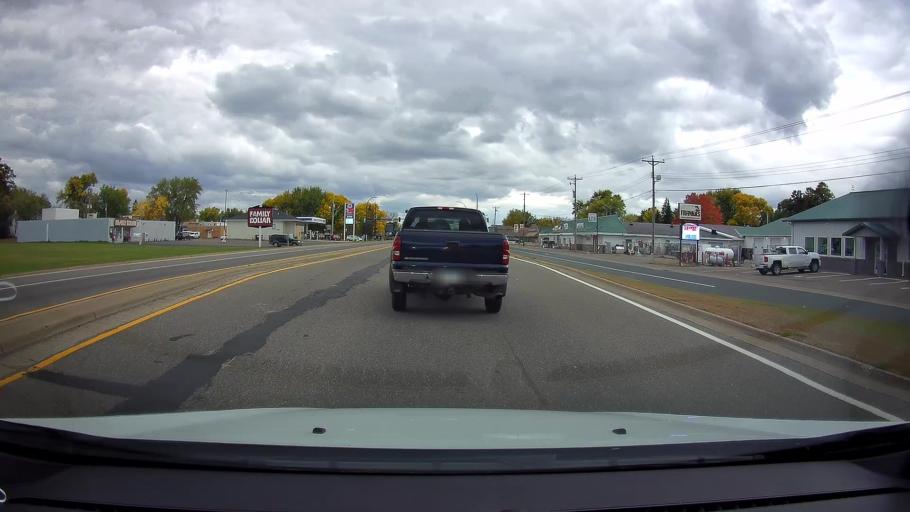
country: US
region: Minnesota
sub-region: Chisago County
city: Chisago City
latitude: 45.3742
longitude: -92.8882
